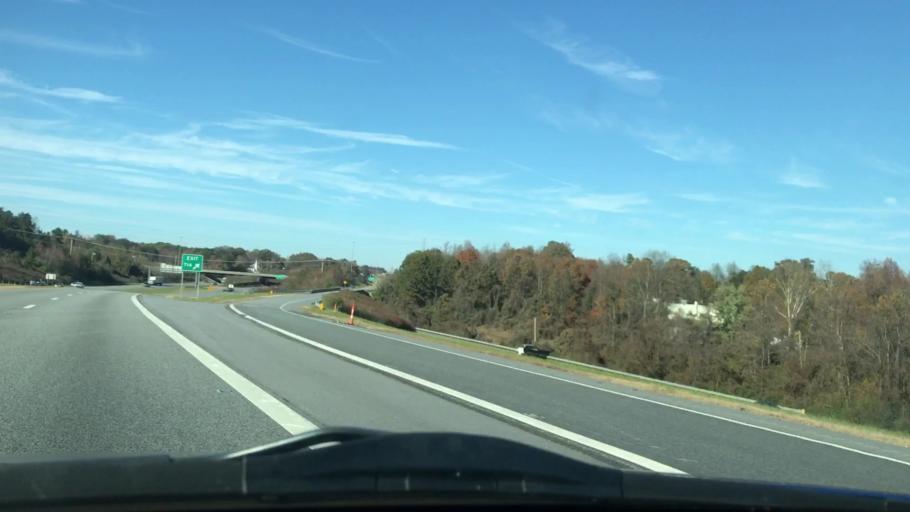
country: US
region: North Carolina
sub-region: Guilford County
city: High Point
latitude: 35.9497
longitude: -79.9744
